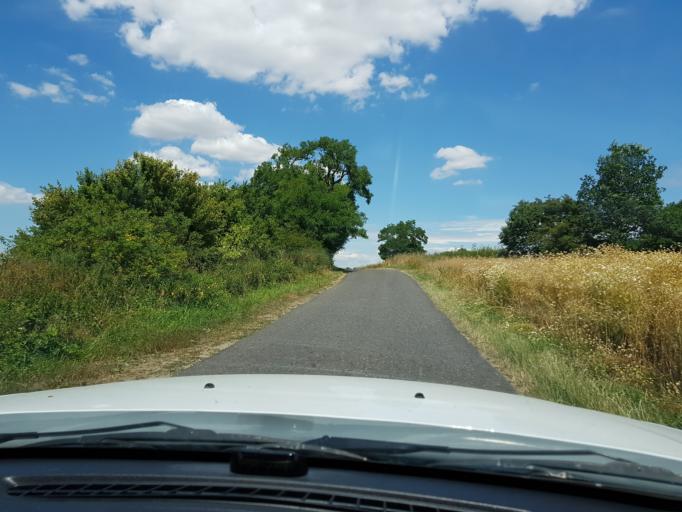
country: PL
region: West Pomeranian Voivodeship
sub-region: Powiat mysliborski
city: Barlinek
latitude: 52.9714
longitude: 15.1252
